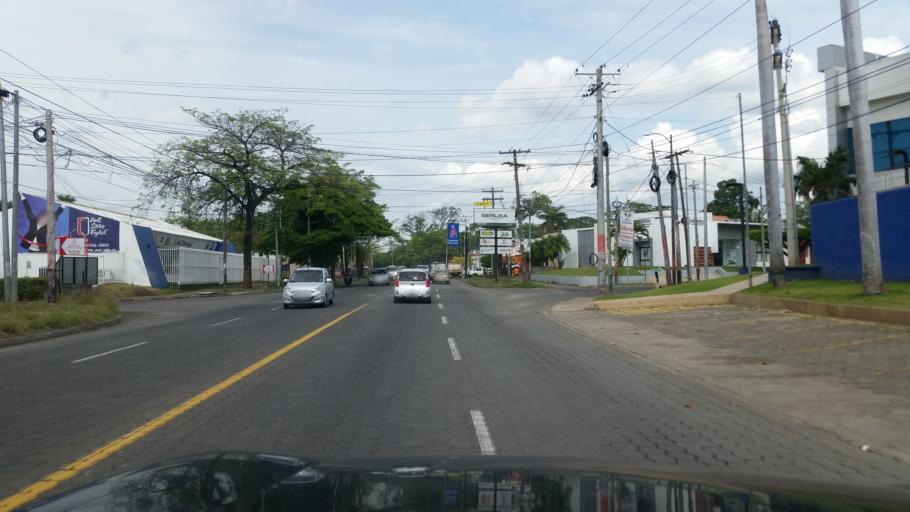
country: NI
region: Managua
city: Managua
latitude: 12.1357
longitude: -86.2855
